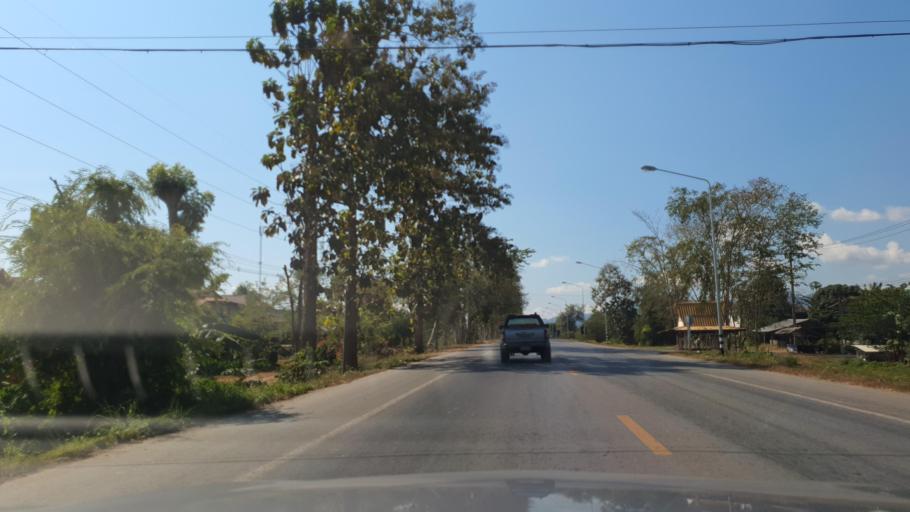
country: TH
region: Nan
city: Tha Wang Pha
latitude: 19.0211
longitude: 100.7911
